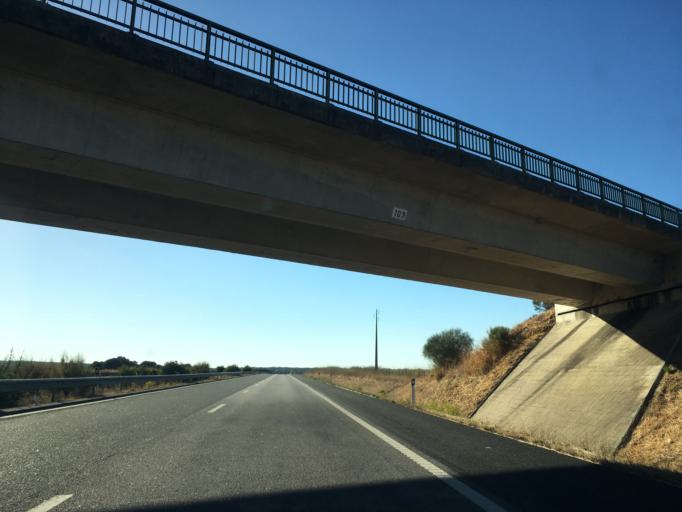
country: PT
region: Evora
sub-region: Evora
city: Evora
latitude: 38.6307
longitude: -7.9309
